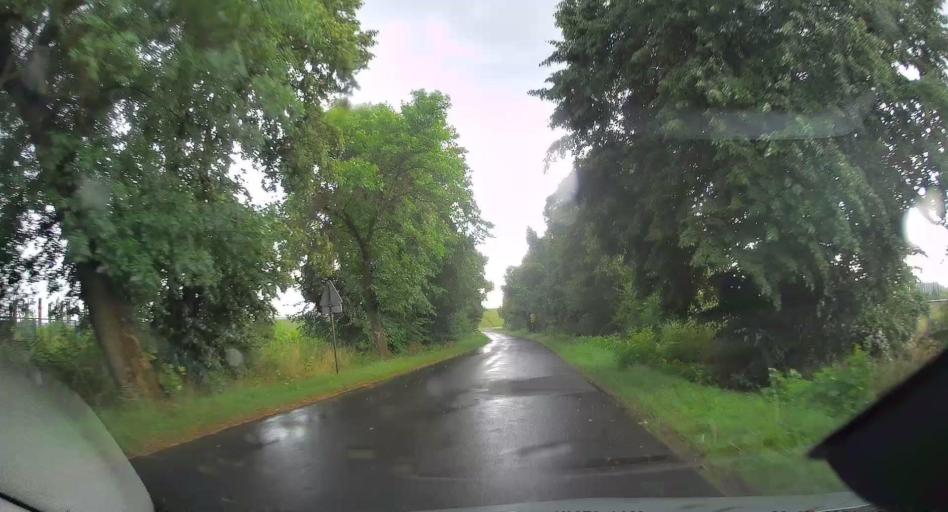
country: PL
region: Lodz Voivodeship
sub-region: Powiat brzezinski
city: Rogow
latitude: 51.8085
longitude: 19.8735
